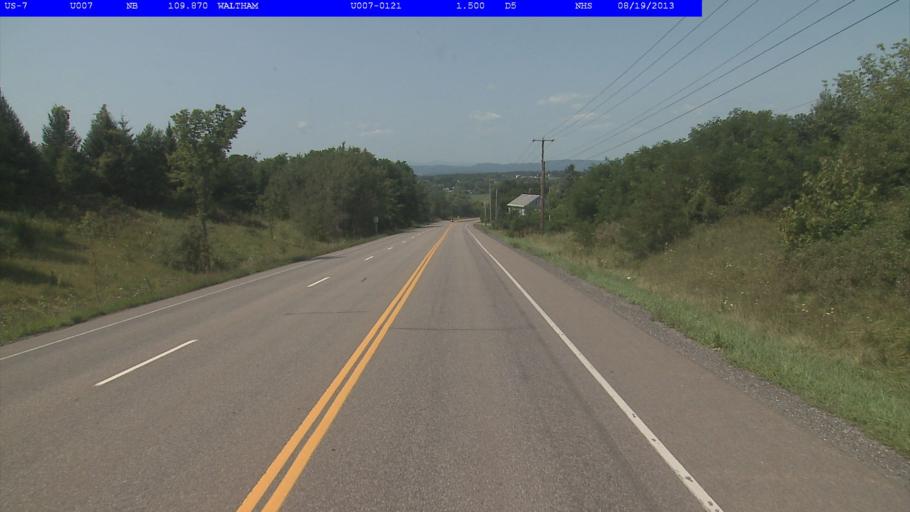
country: US
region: Vermont
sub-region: Addison County
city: Vergennes
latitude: 44.1619
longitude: -73.2326
